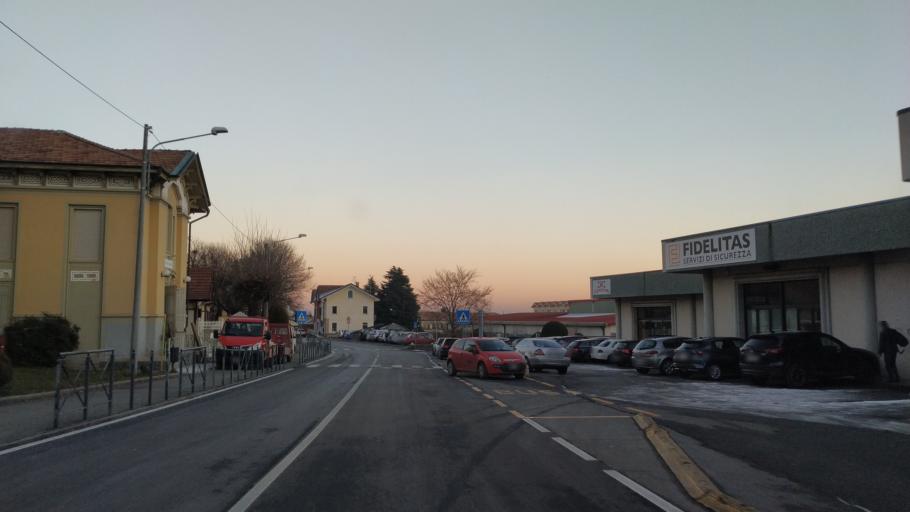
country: IT
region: Piedmont
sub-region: Provincia di Biella
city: Vigliano Biellese
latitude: 45.5594
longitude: 8.0921
